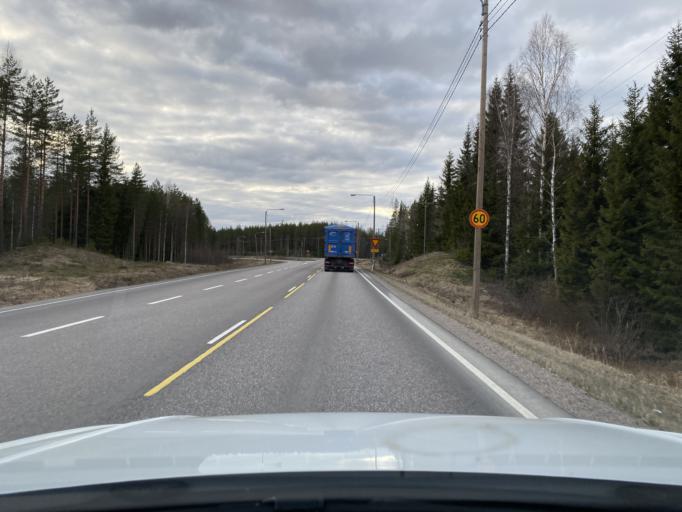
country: FI
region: Uusimaa
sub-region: Helsinki
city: Kaerkoelae
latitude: 60.8267
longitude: 24.0206
